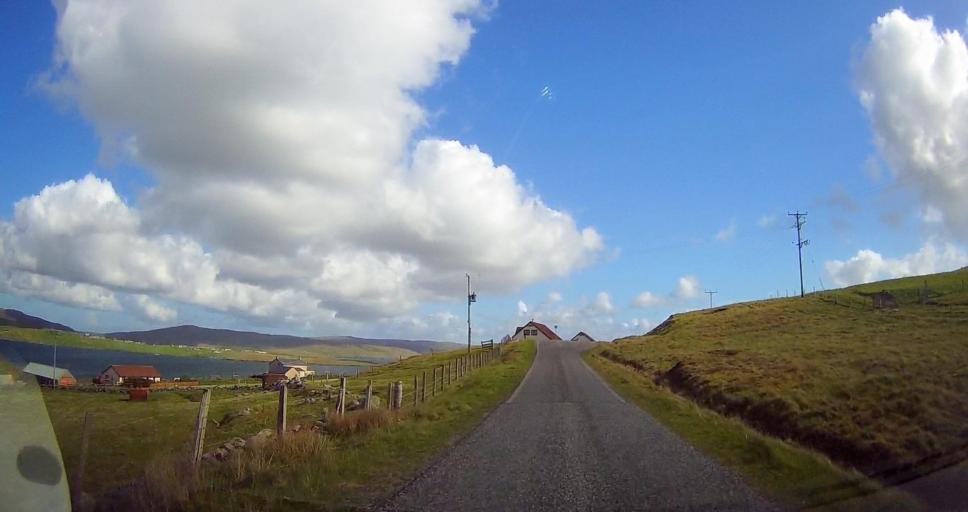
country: GB
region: Scotland
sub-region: Shetland Islands
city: Lerwick
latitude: 60.3841
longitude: -1.3798
